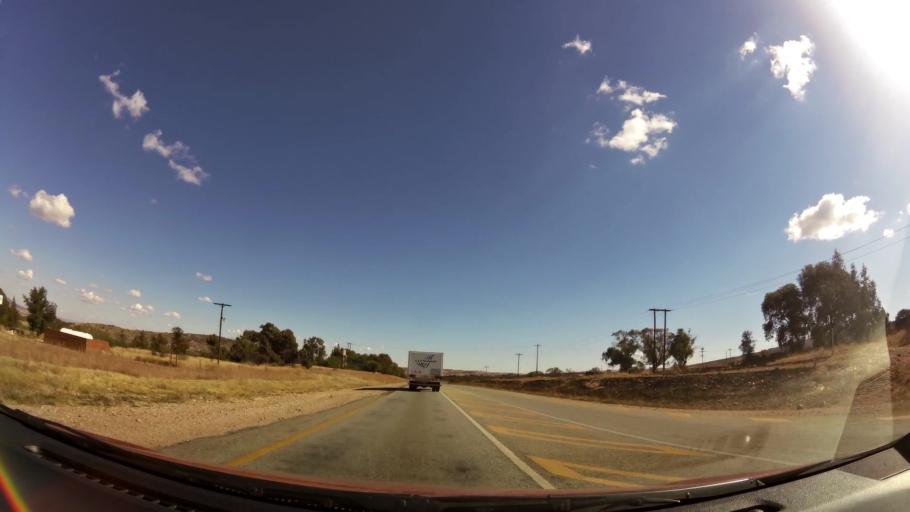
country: ZA
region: North-West
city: Fochville
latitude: -26.4351
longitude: 27.5075
